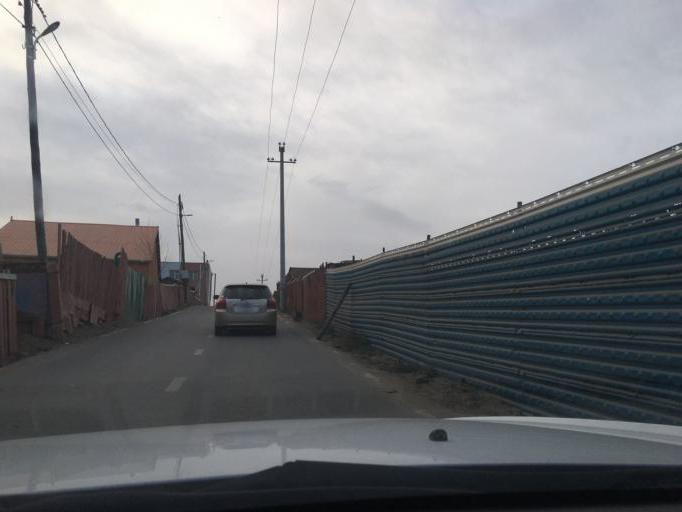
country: MN
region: Ulaanbaatar
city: Ulaanbaatar
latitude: 47.9226
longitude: 106.8489
